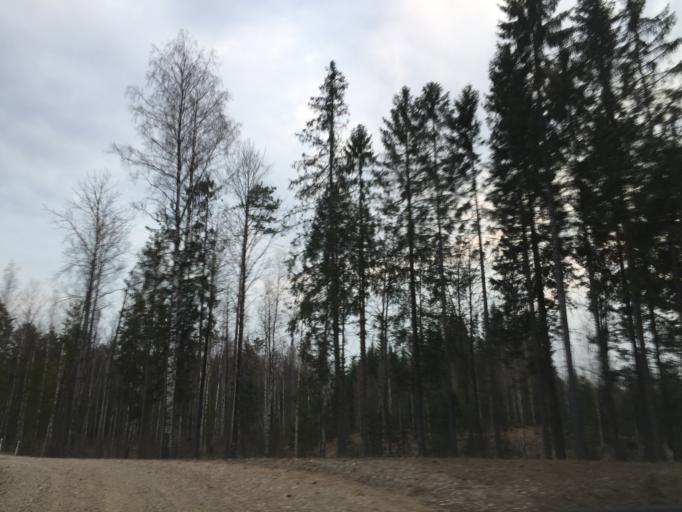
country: LV
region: Raunas
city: Rauna
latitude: 57.1281
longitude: 25.5965
